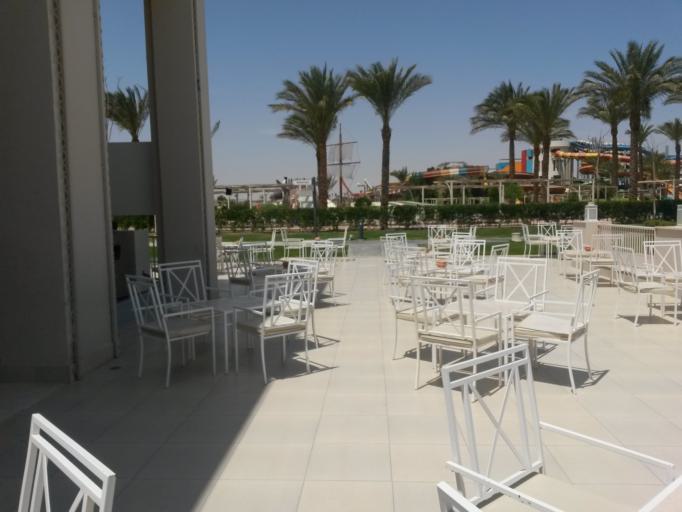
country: EG
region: Red Sea
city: Makadi Bay
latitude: 26.9822
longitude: 33.8739
